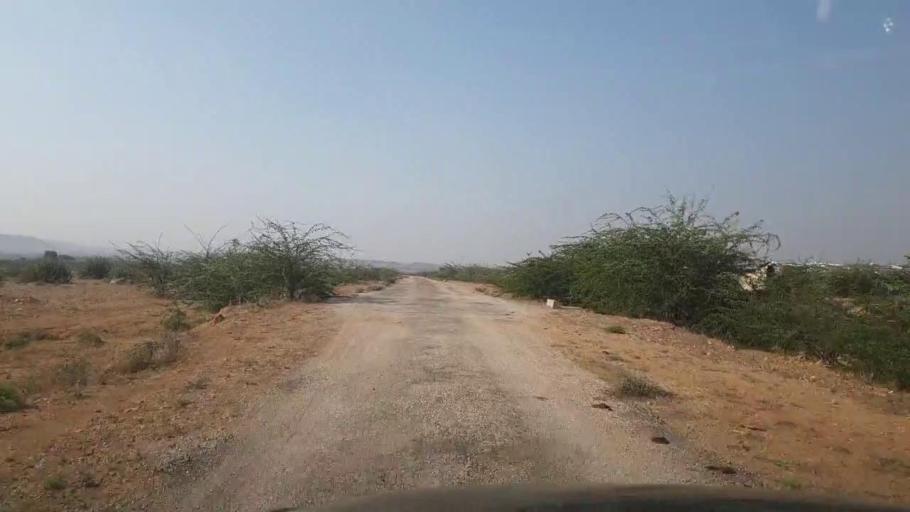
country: PK
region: Sindh
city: Gharo
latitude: 25.0614
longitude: 67.5636
